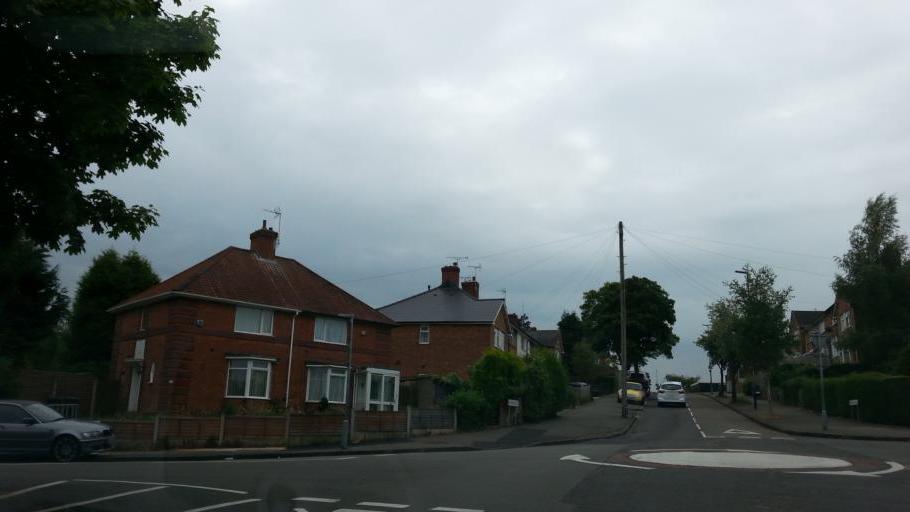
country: GB
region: England
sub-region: Worcestershire
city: Barnt Green
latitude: 52.3936
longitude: -2.0043
